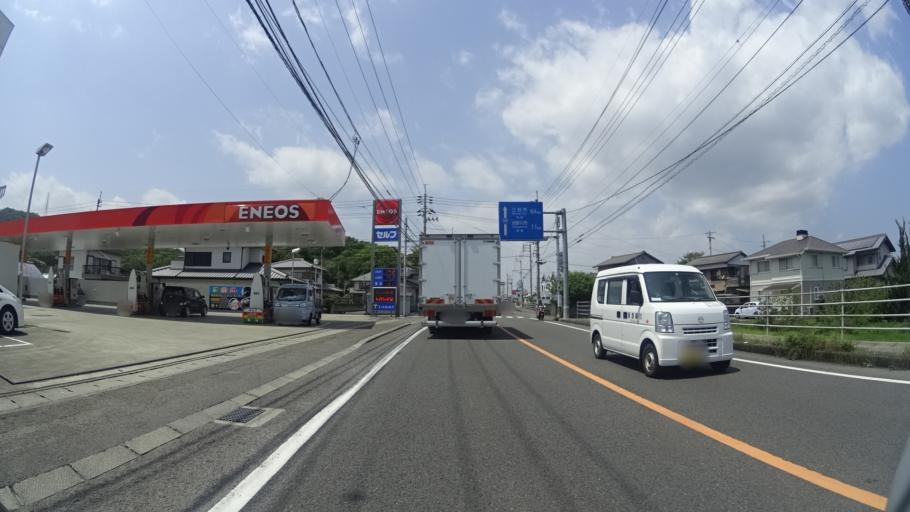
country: JP
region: Tokushima
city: Ishii
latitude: 34.0703
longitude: 134.4679
